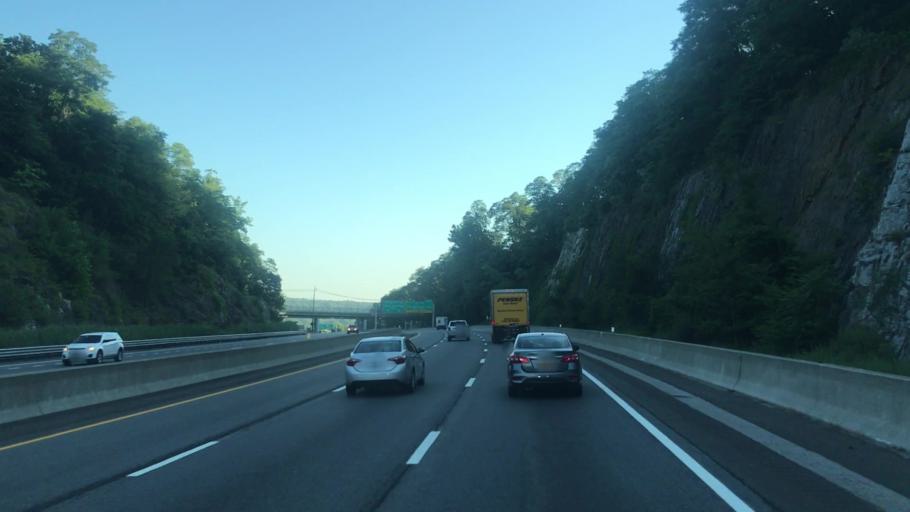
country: US
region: New York
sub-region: Westchester County
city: Elmsford
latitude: 41.0509
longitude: -73.8332
